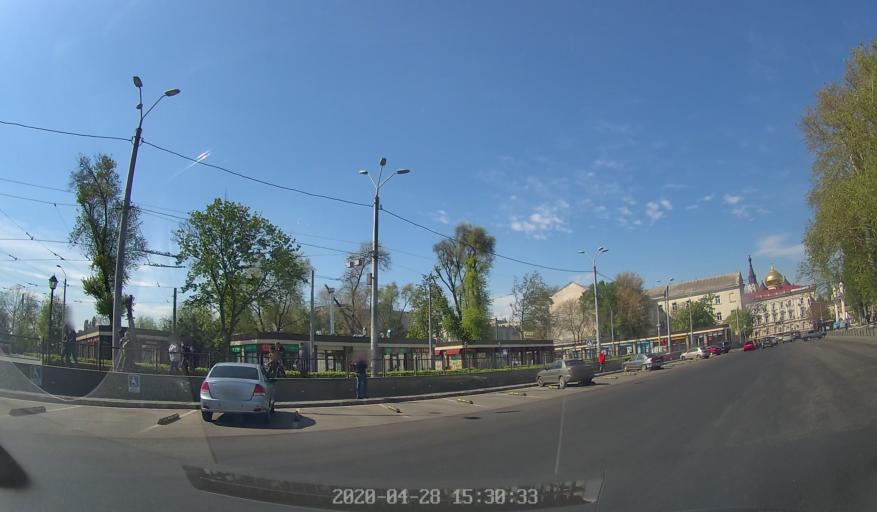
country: NG
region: Niger
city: Lemu
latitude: 9.2934
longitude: 6.1479
